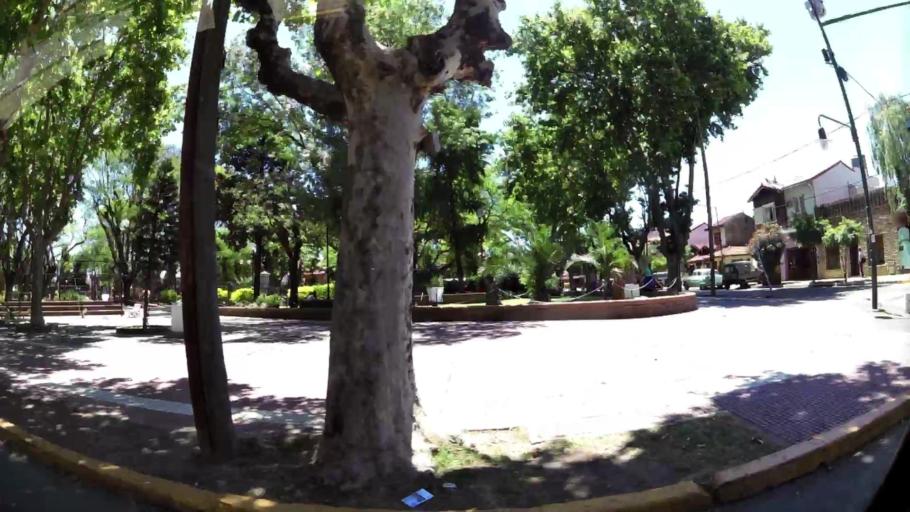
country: AR
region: Buenos Aires
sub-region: Partido de San Isidro
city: San Isidro
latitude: -34.4921
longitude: -58.5097
